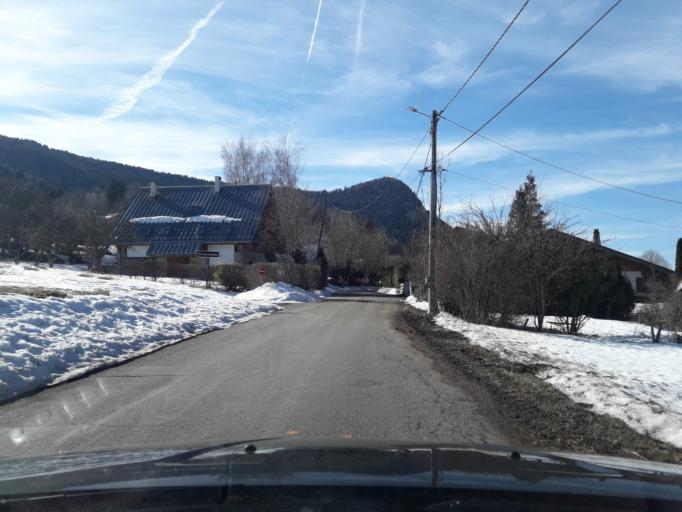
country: FR
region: Rhone-Alpes
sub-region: Departement de l'Isere
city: Le Sappey-en-Chartreuse
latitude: 45.2515
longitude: 5.7698
